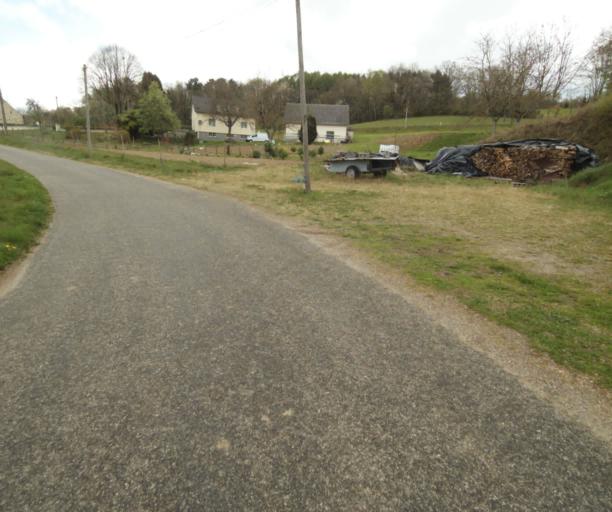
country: FR
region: Limousin
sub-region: Departement de la Correze
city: Laguenne
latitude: 45.2509
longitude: 1.8586
